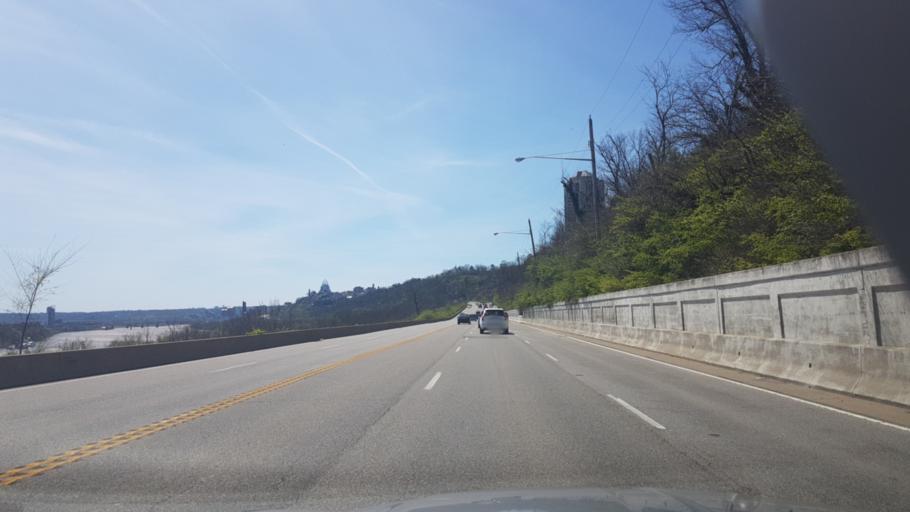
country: US
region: Kentucky
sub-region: Campbell County
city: Dayton
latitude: 39.1228
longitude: -84.4755
